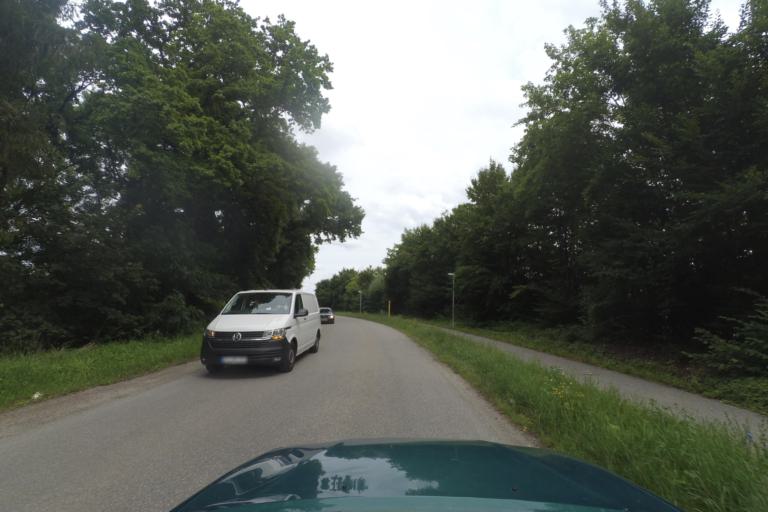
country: DE
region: Bavaria
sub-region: Lower Bavaria
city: Mamming
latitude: 48.6559
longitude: 12.6136
